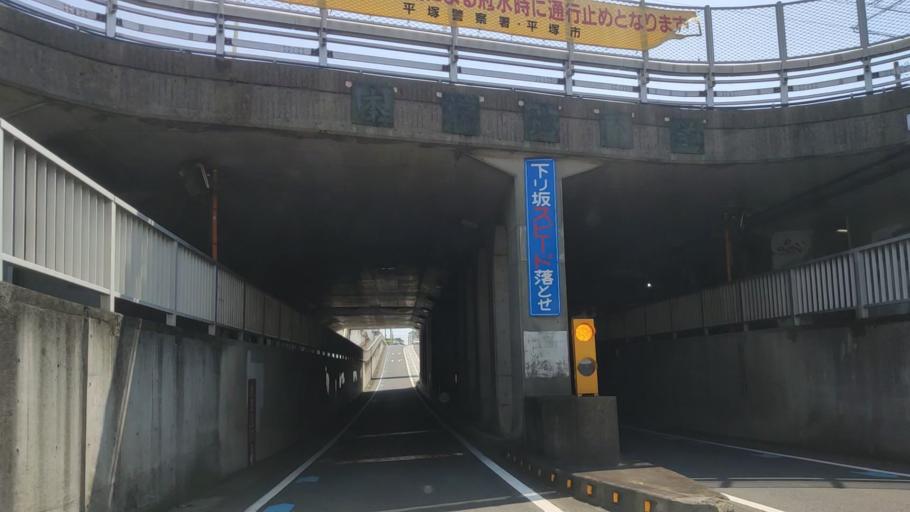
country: JP
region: Kanagawa
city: Hiratsuka
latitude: 35.3254
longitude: 139.3377
